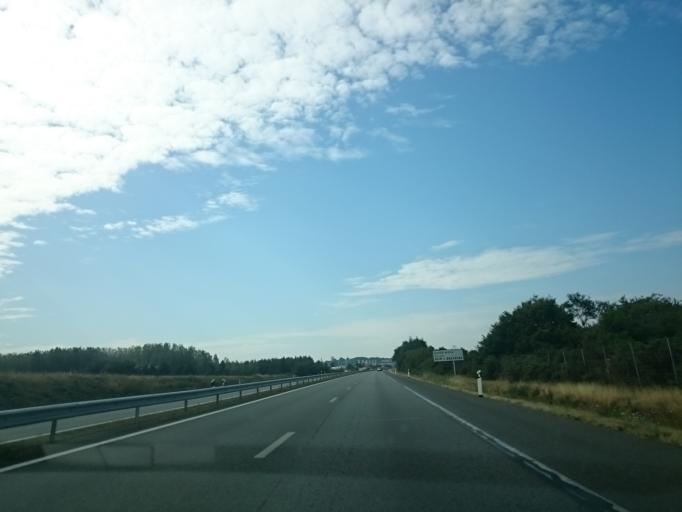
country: FR
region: Brittany
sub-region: Departement d'Ille-et-Vilaine
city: Bain-de-Bretagne
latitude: 47.8656
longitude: -1.6911
